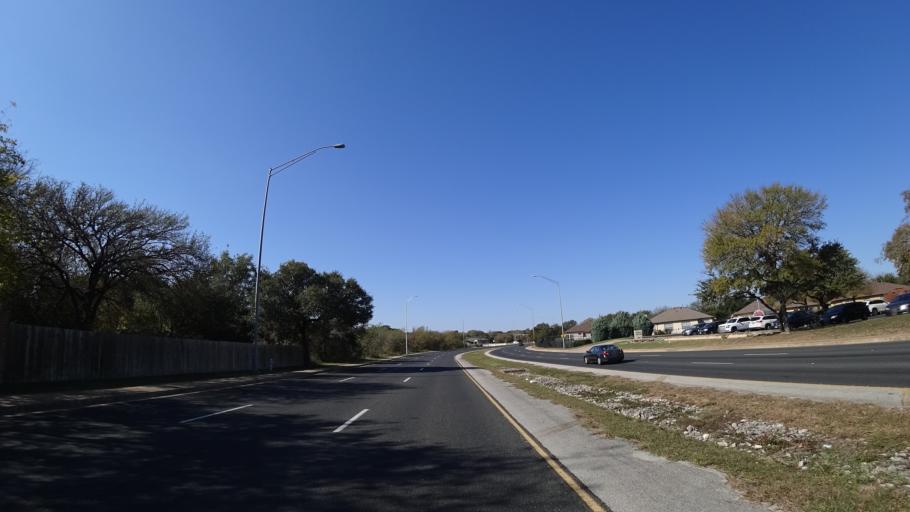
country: US
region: Texas
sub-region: Travis County
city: Shady Hollow
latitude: 30.2247
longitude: -97.8525
